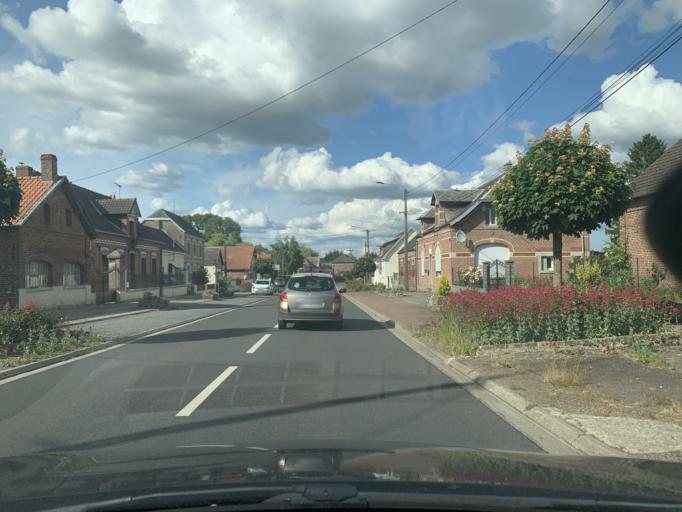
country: FR
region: Picardie
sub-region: Departement de la Somme
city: Moislains
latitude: 50.0067
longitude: 3.0191
